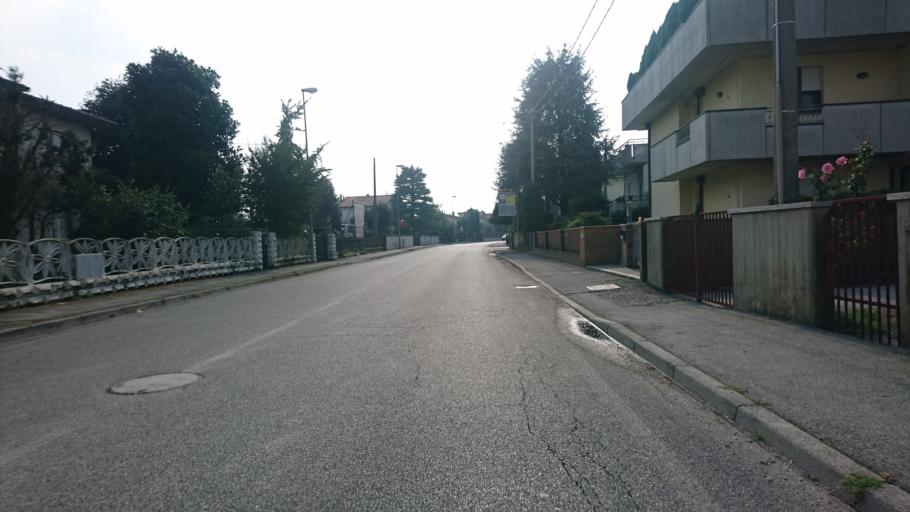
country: IT
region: Veneto
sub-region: Provincia di Rovigo
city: Rovigo
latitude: 45.0593
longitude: 11.7822
